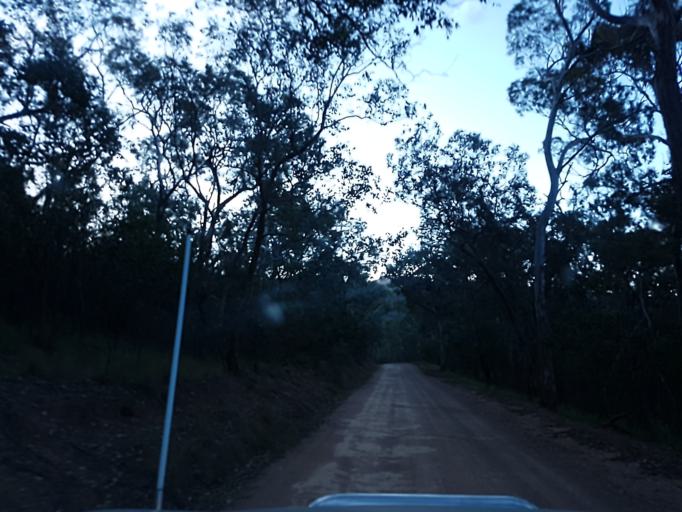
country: AU
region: Victoria
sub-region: Wellington
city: Heyfield
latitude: -37.4059
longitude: 147.0757
